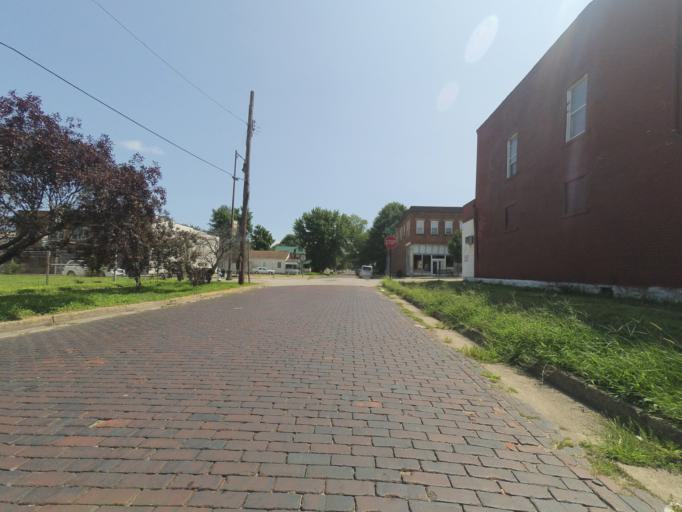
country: US
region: West Virginia
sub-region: Cabell County
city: Huntington
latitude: 38.4102
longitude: -82.4794
